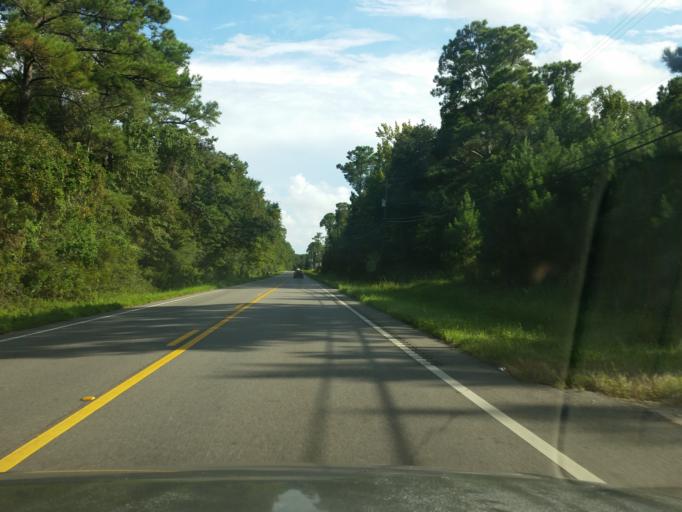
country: US
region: Alabama
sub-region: Mobile County
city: Theodore
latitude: 30.4338
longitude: -88.1087
